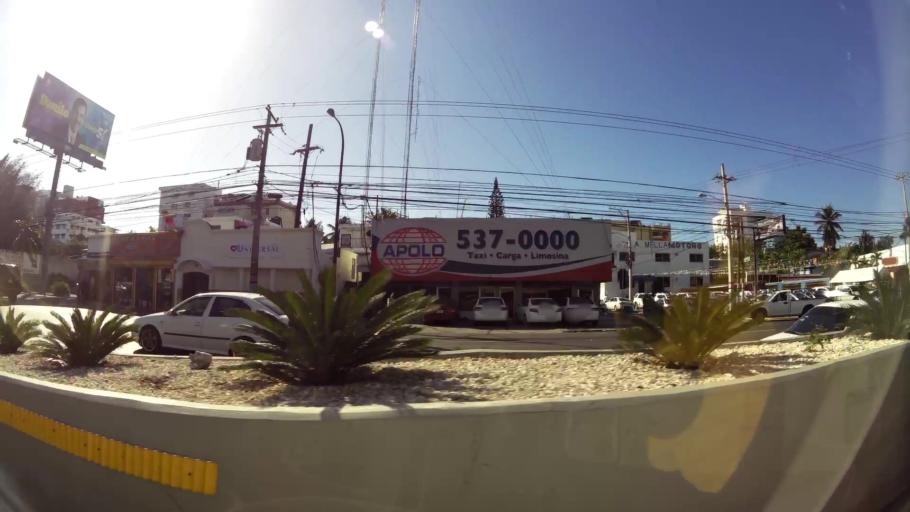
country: DO
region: Nacional
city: Bella Vista
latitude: 18.4529
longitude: -69.9587
